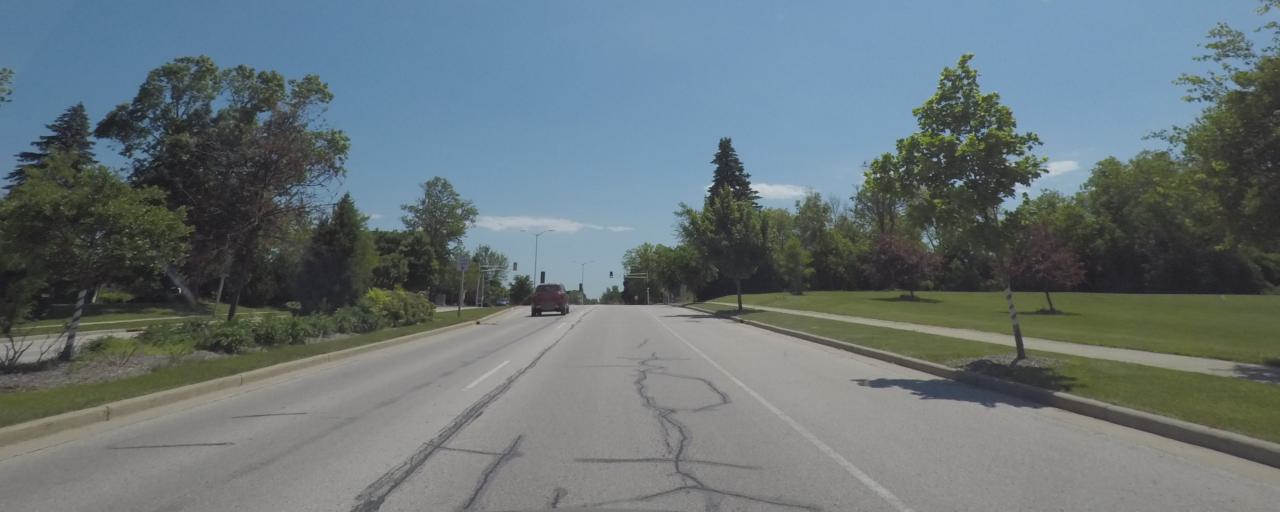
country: US
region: Wisconsin
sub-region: Waukesha County
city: Brookfield
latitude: 43.0328
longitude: -88.1271
